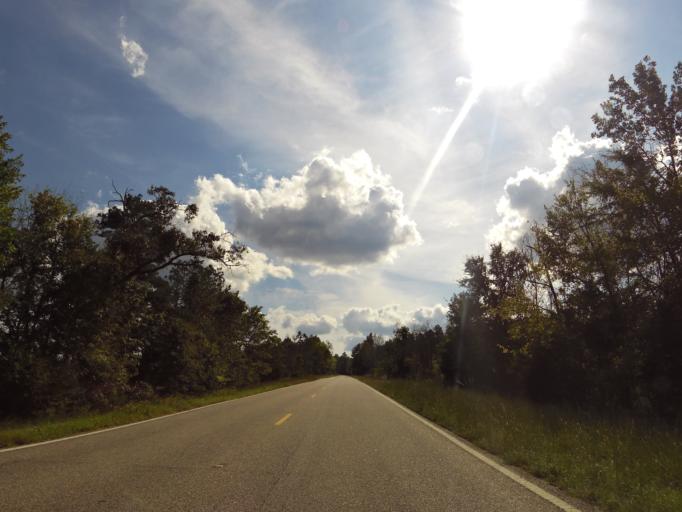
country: US
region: Alabama
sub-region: Dallas County
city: Selmont-West Selmont
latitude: 32.1720
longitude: -87.0520
